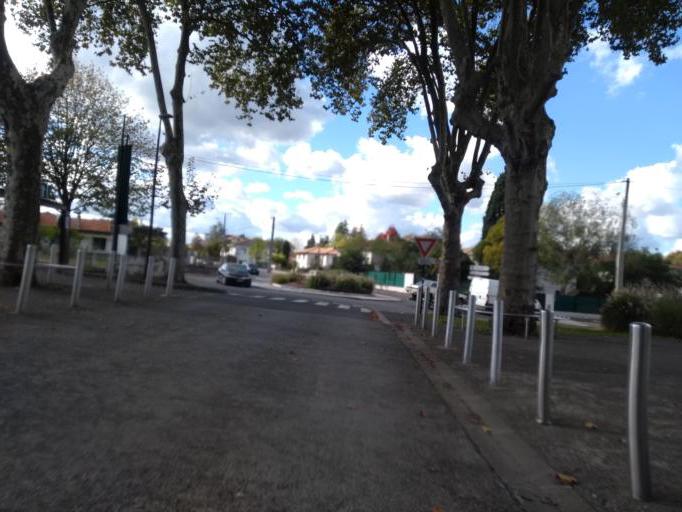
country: FR
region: Aquitaine
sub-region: Departement de la Gironde
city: Gradignan
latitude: 44.7678
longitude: -0.6111
